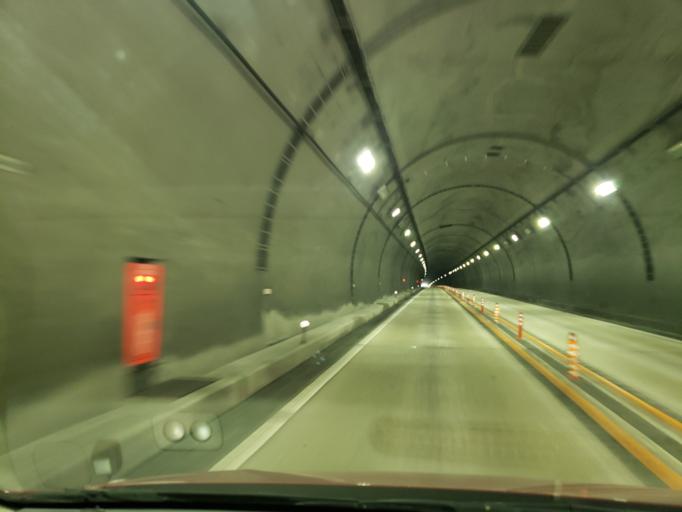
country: JP
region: Tokushima
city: Kamojimacho-jogejima
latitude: 34.1136
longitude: 134.3218
